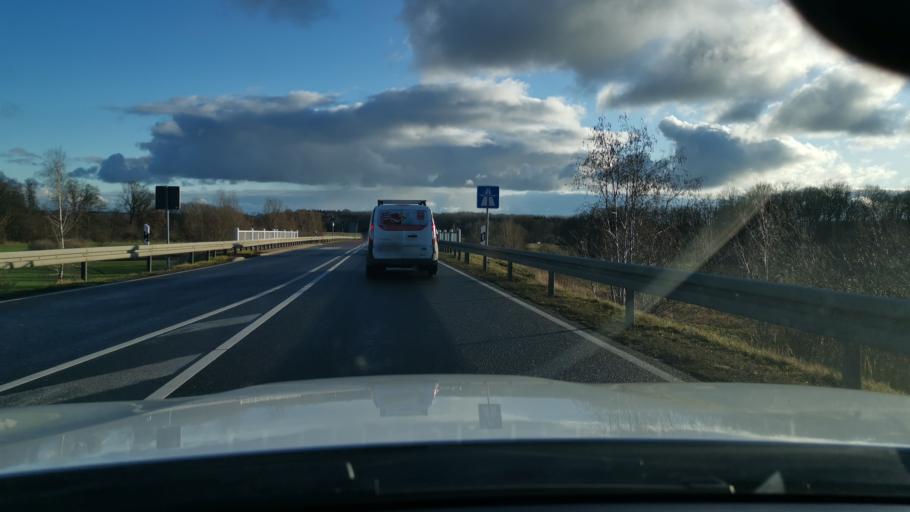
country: DE
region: Mecklenburg-Vorpommern
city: Tessin
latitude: 54.0397
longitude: 12.4089
